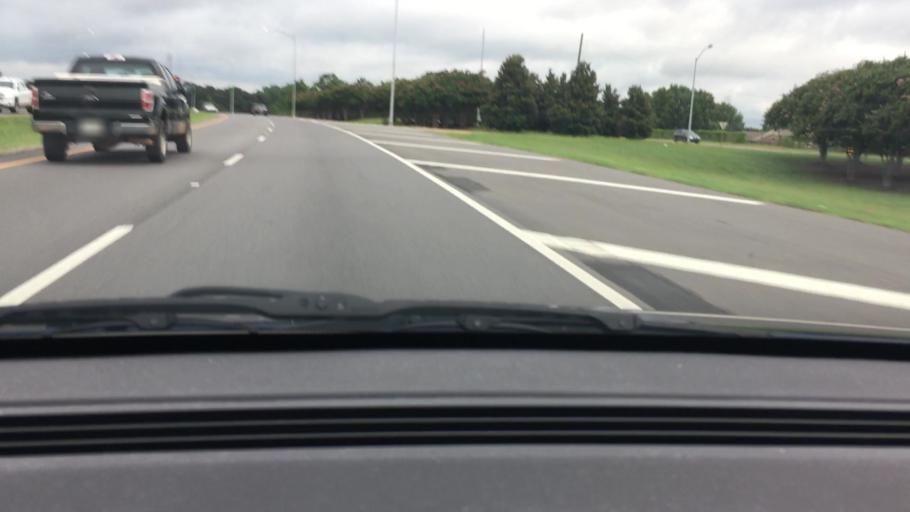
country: US
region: Alabama
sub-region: Tuscaloosa County
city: Tuscaloosa
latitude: 33.2120
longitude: -87.5253
